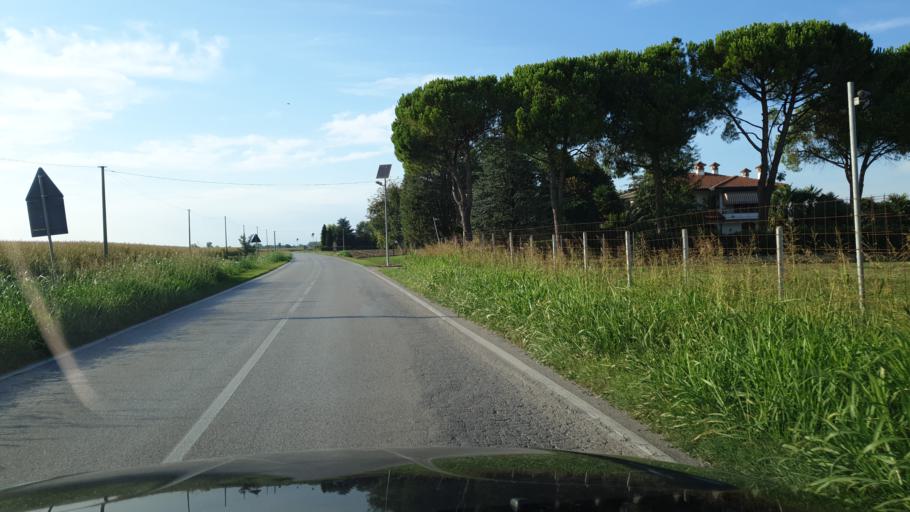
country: IT
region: Veneto
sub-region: Provincia di Rovigo
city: Fiesso Umbertiano
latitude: 44.9713
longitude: 11.6106
